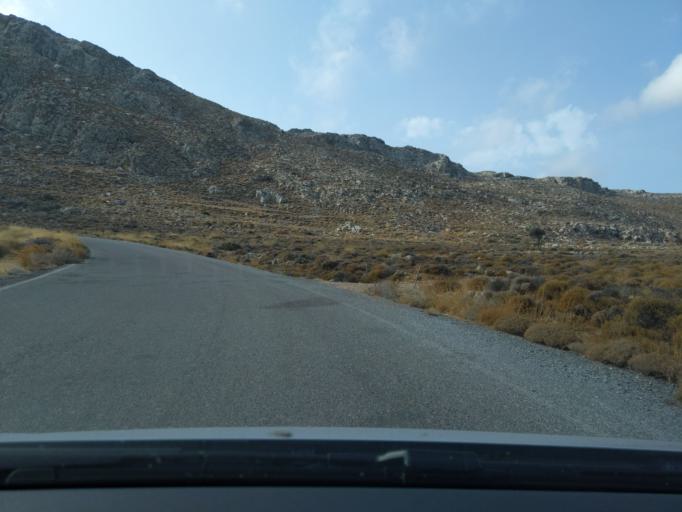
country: GR
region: Crete
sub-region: Nomos Lasithiou
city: Palekastro
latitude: 35.0908
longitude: 26.2619
